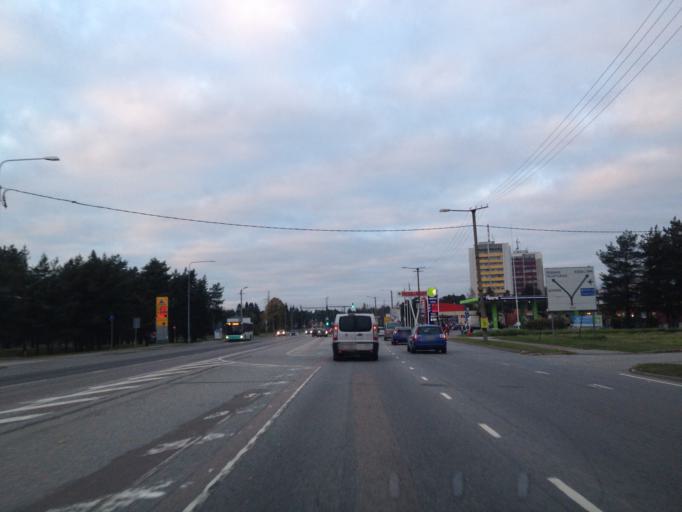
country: EE
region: Harju
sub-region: Saue vald
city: Laagri
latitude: 59.3590
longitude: 24.6304
